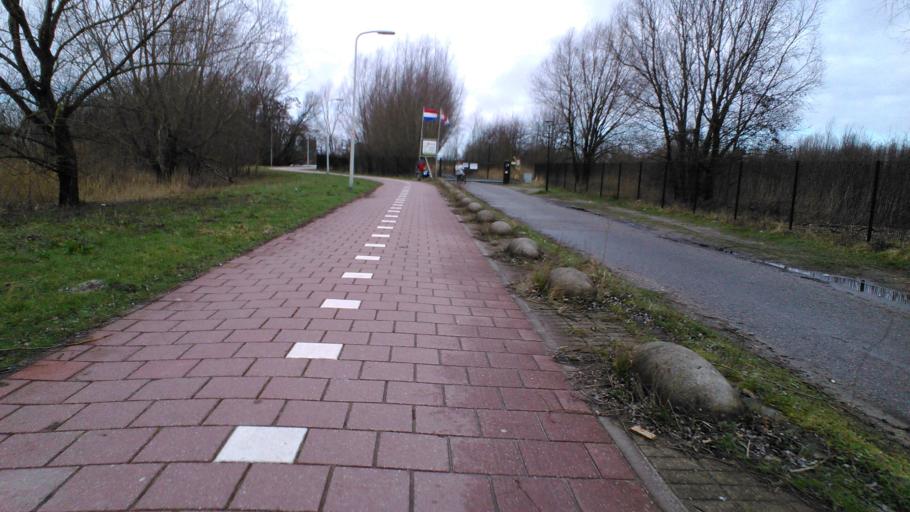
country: NL
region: South Holland
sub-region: Gemeente Den Haag
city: Ypenburg
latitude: 52.0539
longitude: 4.3793
